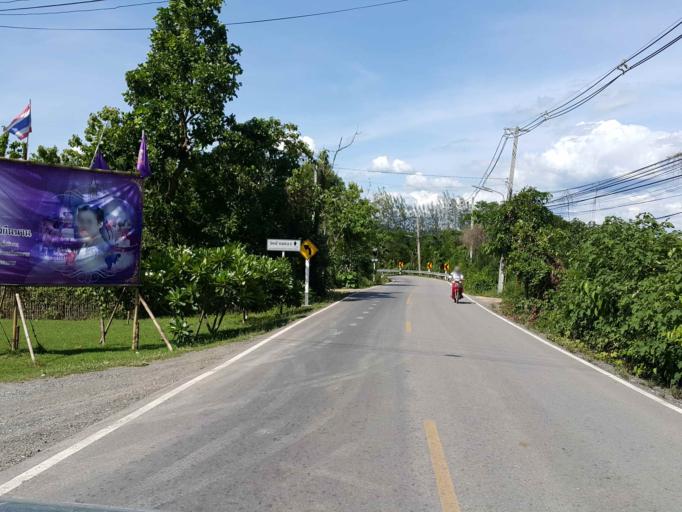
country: TH
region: Chiang Mai
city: San Kamphaeng
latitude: 18.7724
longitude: 99.1546
